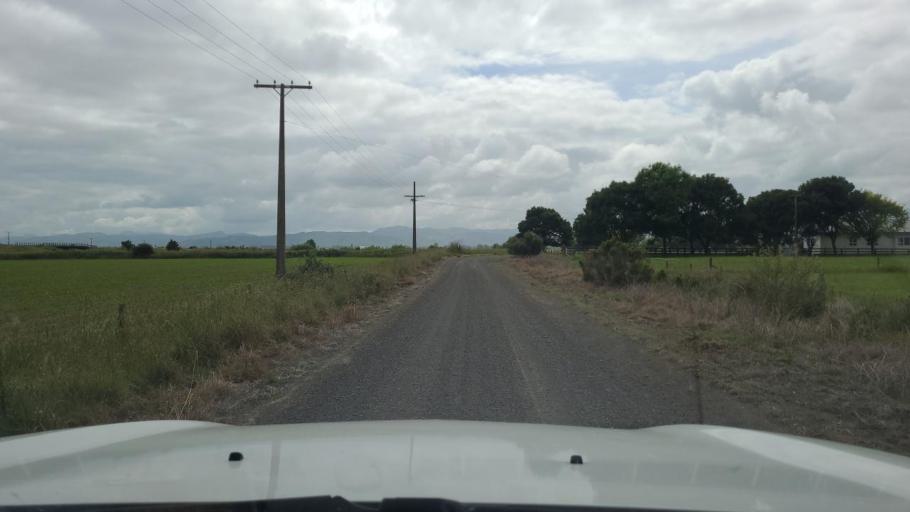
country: NZ
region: Waikato
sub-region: Hauraki District
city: Paeroa
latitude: -37.4996
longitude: 175.5647
